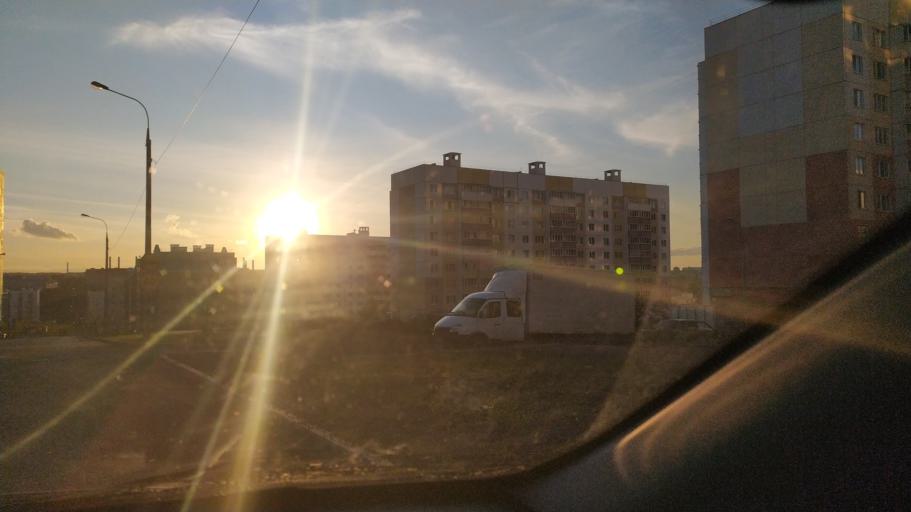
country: RU
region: Chuvashia
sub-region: Cheboksarskiy Rayon
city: Cheboksary
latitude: 56.1163
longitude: 47.2193
